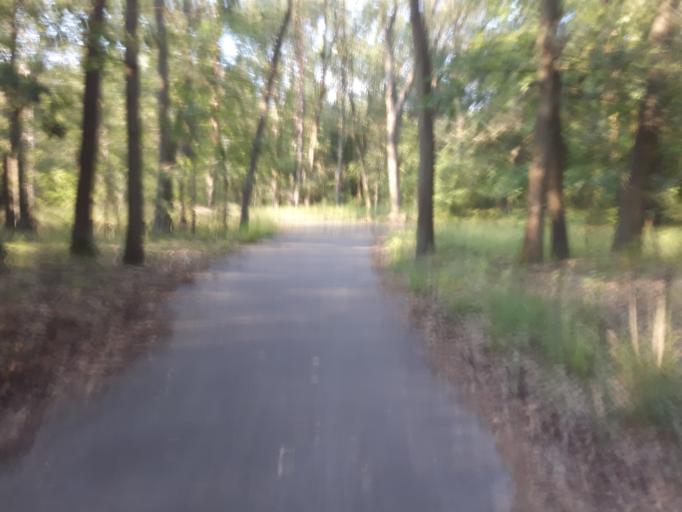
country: DE
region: Berlin
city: Falkenhagener Feld
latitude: 52.5673
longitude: 13.1504
